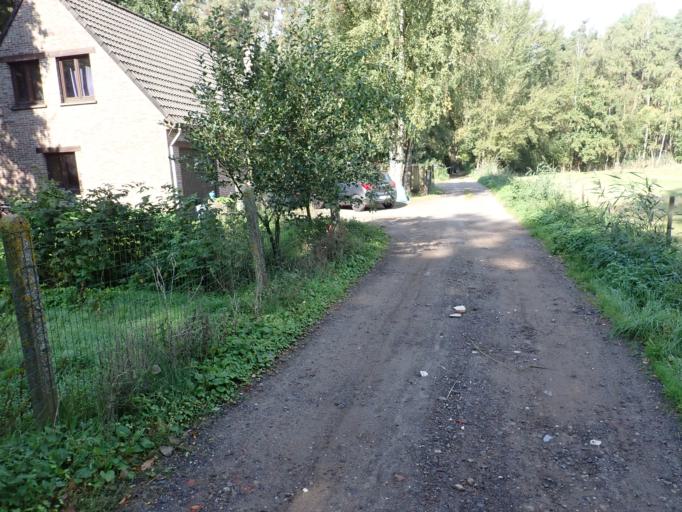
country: BE
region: Flanders
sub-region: Provincie Oost-Vlaanderen
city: Stekene
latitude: 51.2333
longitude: 4.0695
